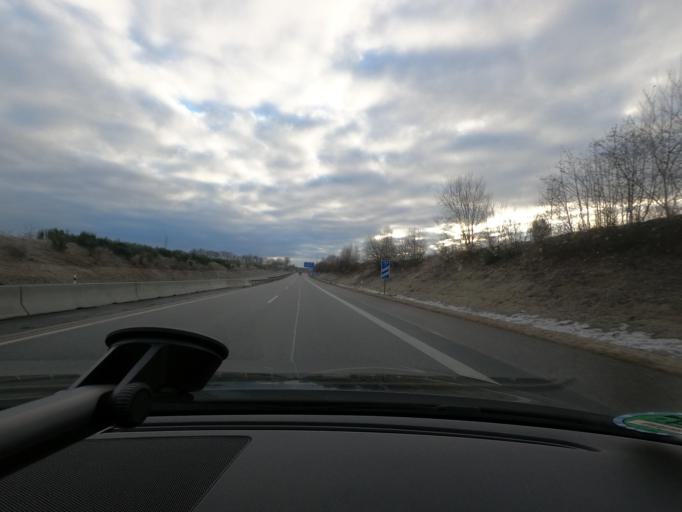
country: DE
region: Thuringia
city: Sankt Kilian
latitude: 50.5195
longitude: 10.7605
